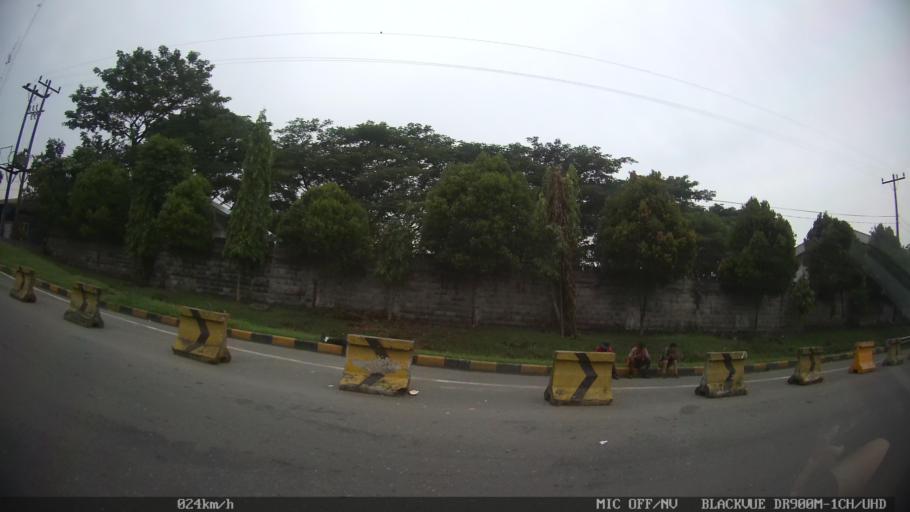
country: ID
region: North Sumatra
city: Deli Tua
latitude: 3.5369
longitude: 98.7217
